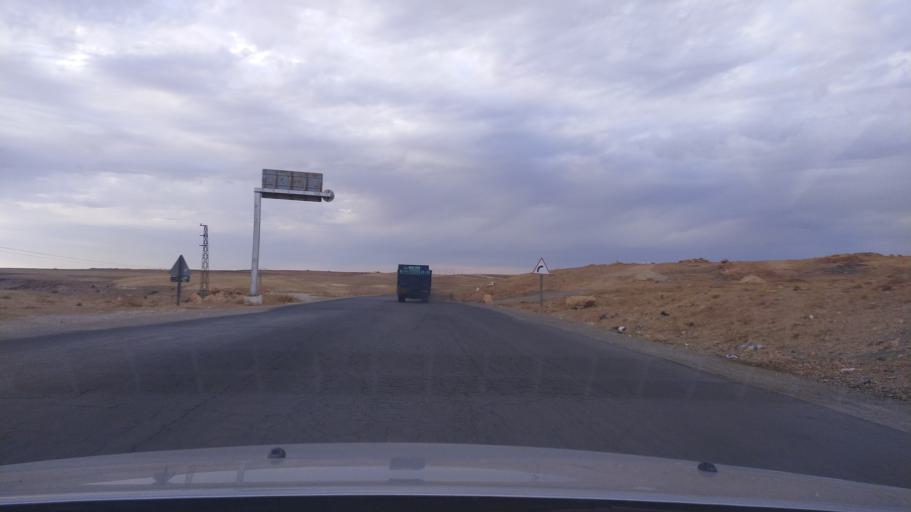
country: DZ
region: Tiaret
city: Frenda
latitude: 34.9934
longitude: 1.1291
